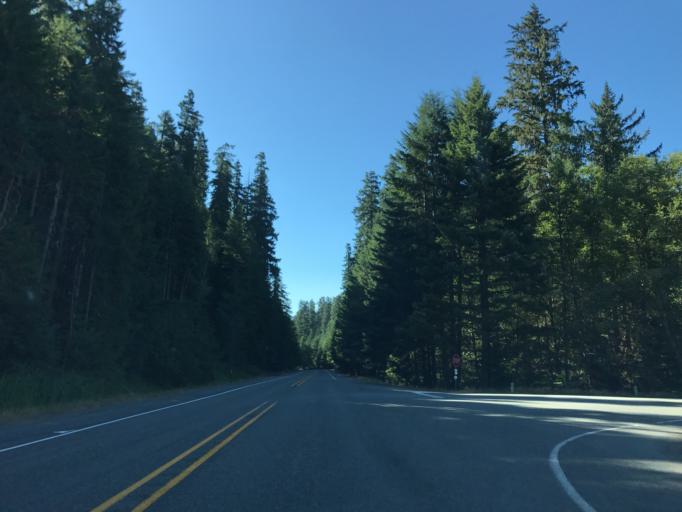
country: US
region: Washington
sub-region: King County
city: Riverbend
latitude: 47.0826
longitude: -121.5827
